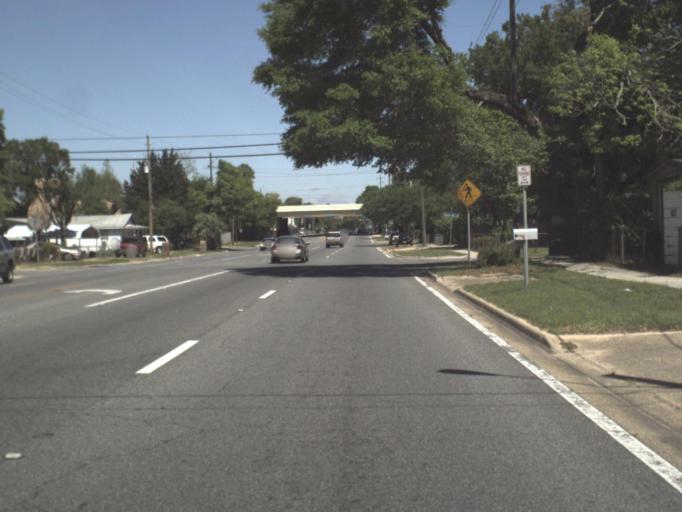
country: US
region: Florida
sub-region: Escambia County
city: Goulding
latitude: 30.4463
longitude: -87.2205
